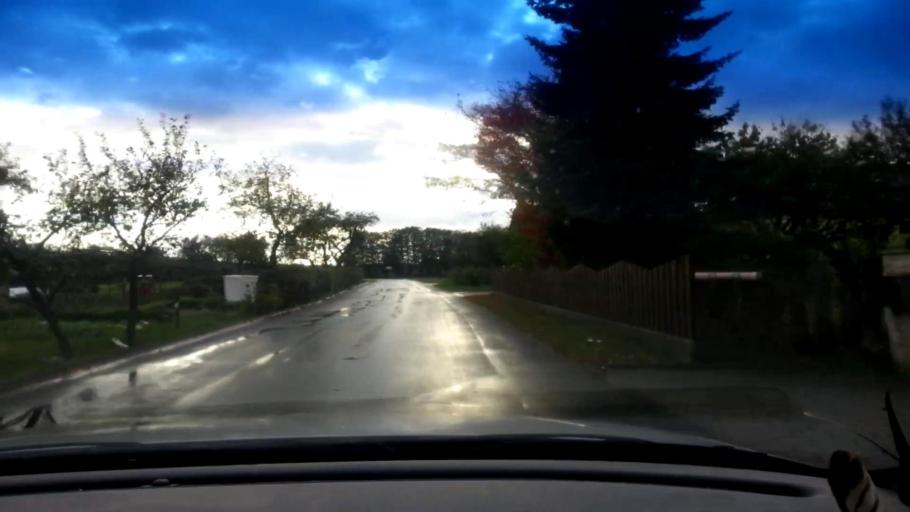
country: DE
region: Bavaria
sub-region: Upper Franconia
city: Burgebrach
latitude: 49.8239
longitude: 10.6965
